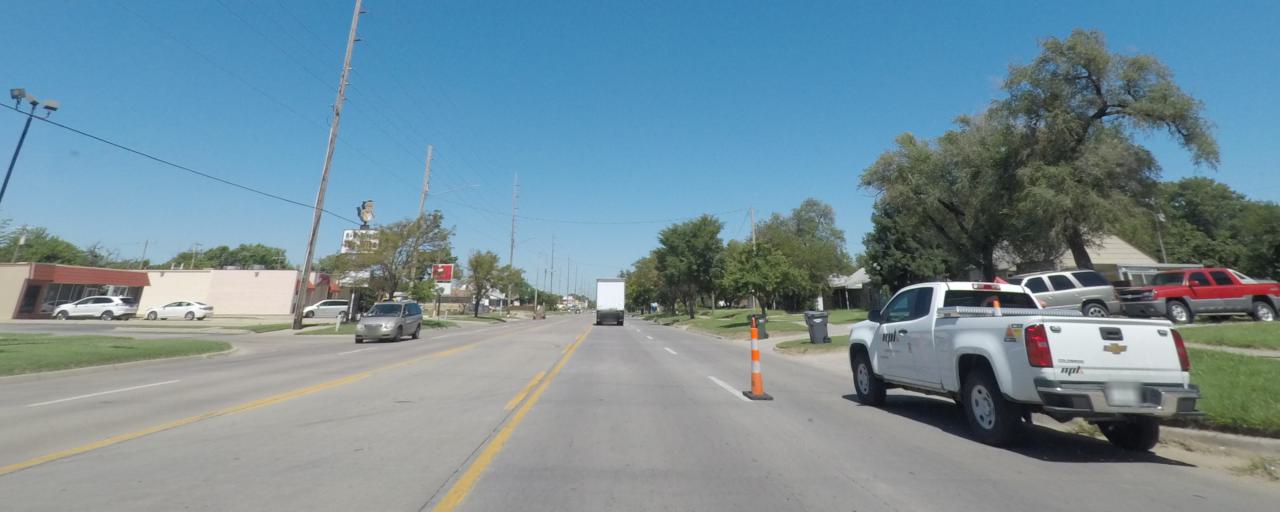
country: US
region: Kansas
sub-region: Sedgwick County
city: Wichita
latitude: 37.6541
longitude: -97.3527
